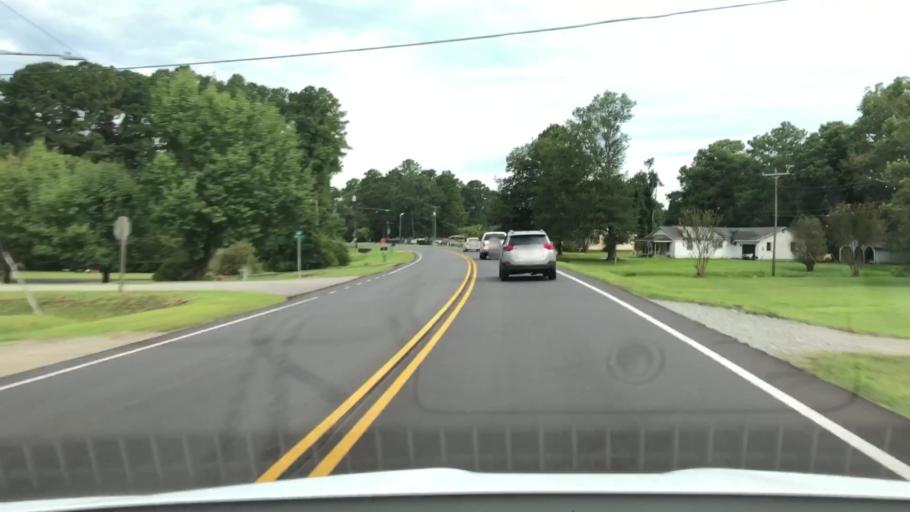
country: US
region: North Carolina
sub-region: Jones County
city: Maysville
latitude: 34.9002
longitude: -77.2236
